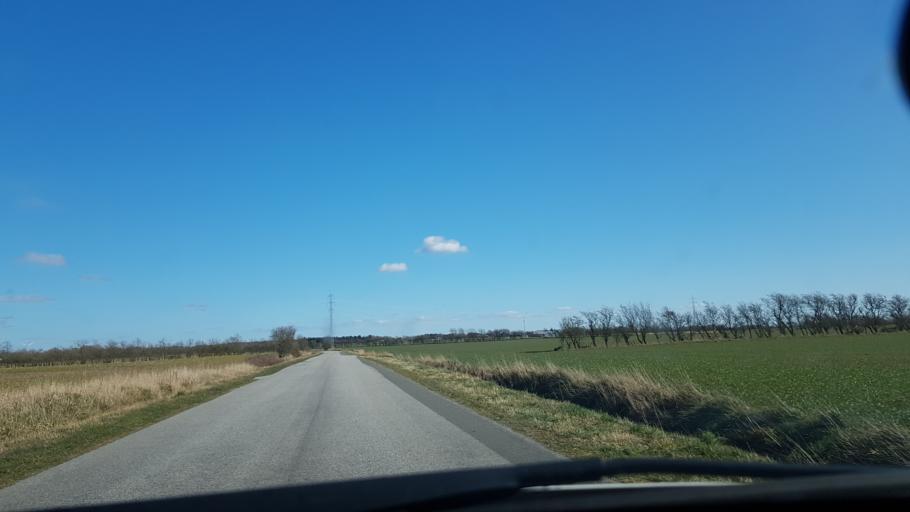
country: DK
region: South Denmark
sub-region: Tonder Kommune
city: Sherrebek
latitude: 55.2227
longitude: 8.8113
